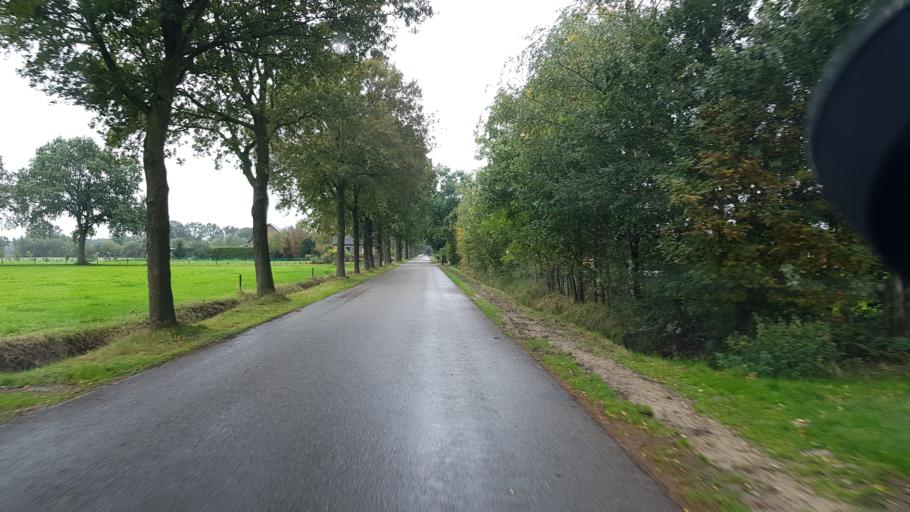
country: NL
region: Gelderland
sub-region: Gemeente Apeldoorn
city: Apeldoorn
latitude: 52.1871
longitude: 6.0309
